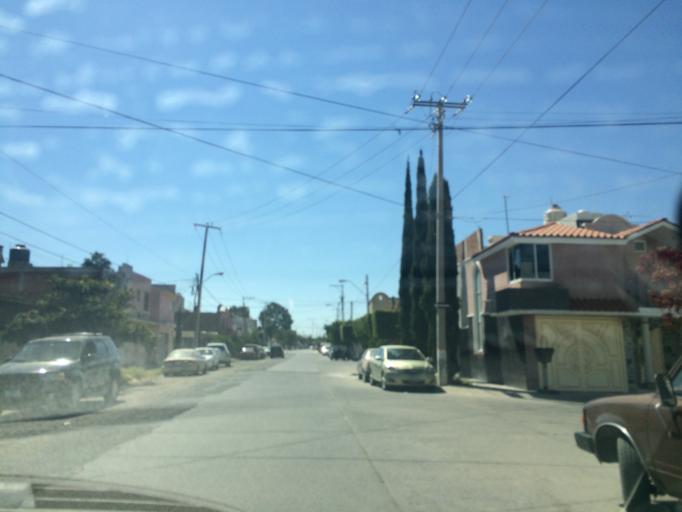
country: MX
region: Guanajuato
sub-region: Leon
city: San Jose de Duran (Los Troncoso)
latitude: 21.0891
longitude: -101.6496
